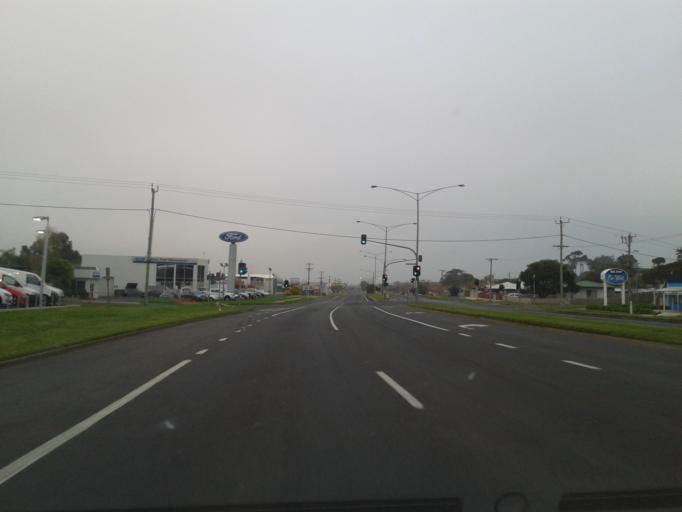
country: AU
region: Victoria
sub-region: Warrnambool
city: Warrnambool
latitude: -38.3700
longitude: 142.4691
